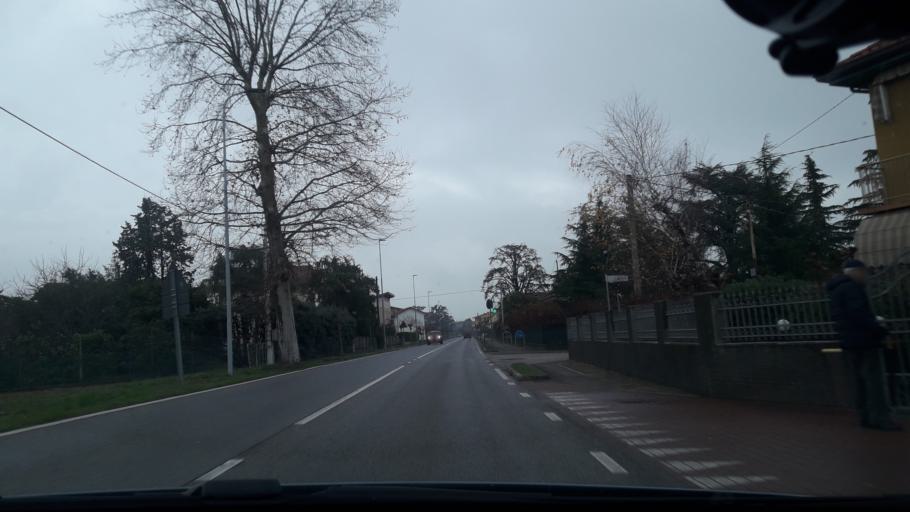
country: IT
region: Friuli Venezia Giulia
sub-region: Provincia di Udine
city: Zugliano-Terenzano-Cargnacco
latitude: 46.0132
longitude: 13.2104
